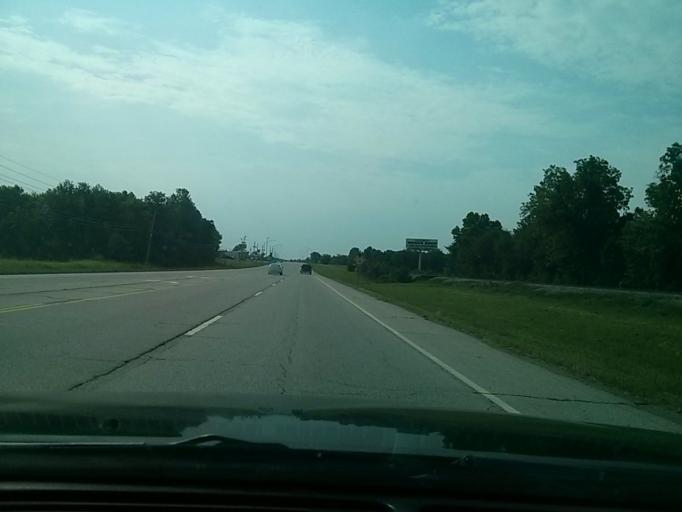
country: US
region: Oklahoma
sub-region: Wagoner County
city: Coweta
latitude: 35.9720
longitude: -95.6605
